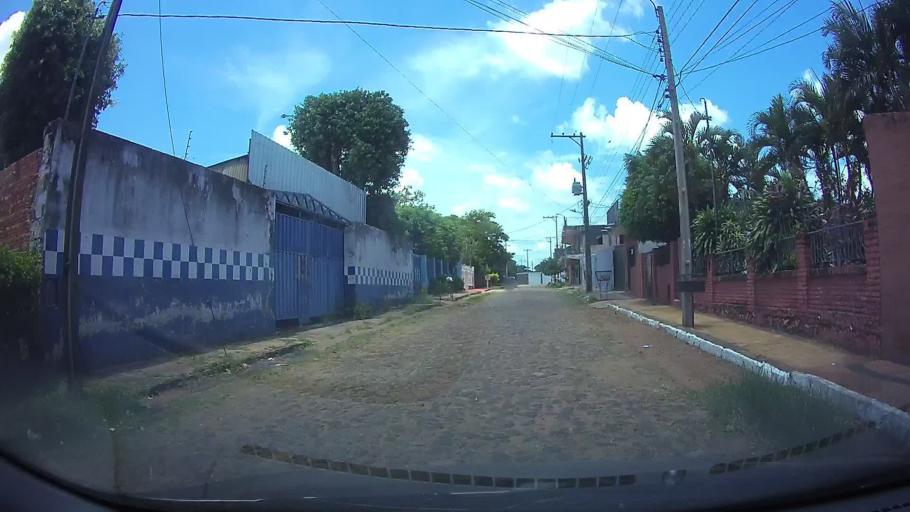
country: PY
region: Central
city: San Lorenzo
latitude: -25.2594
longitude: -57.4854
